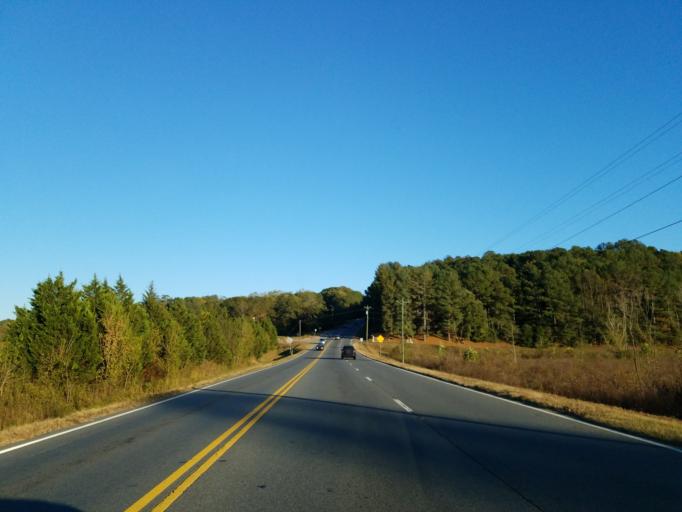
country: US
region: Georgia
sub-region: Dawson County
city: Dawsonville
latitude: 34.3816
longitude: -84.0624
